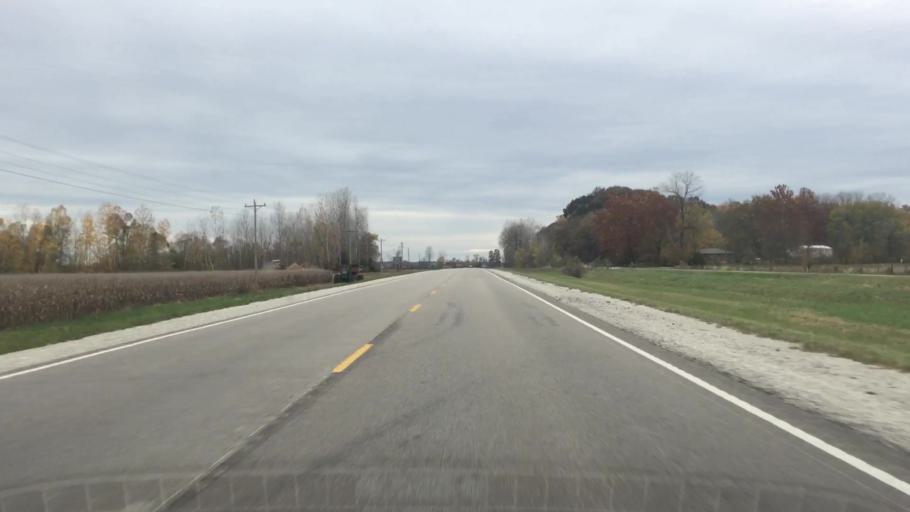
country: US
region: Missouri
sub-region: Callaway County
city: Holts Summit
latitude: 38.5824
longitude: -92.1079
